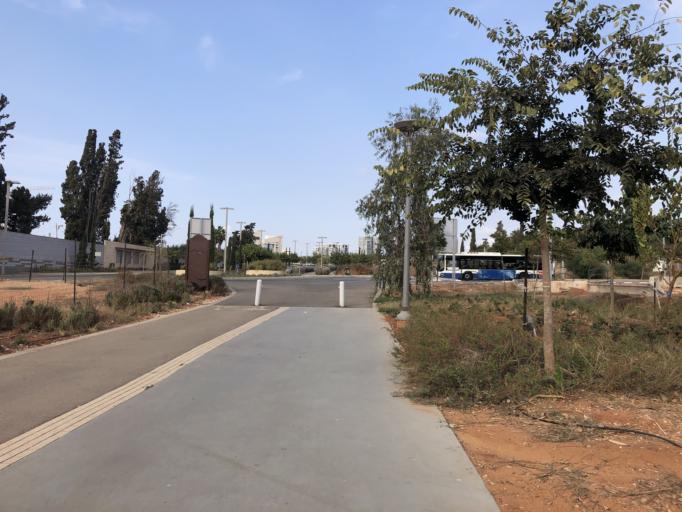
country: IL
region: Tel Aviv
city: Giv`at Shemu'el
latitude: 32.0587
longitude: 34.8453
